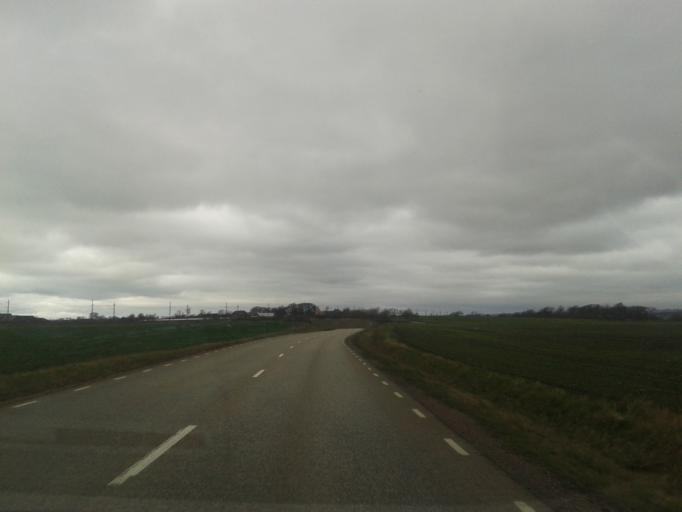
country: SE
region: Skane
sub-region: Bastads Kommun
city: Forslov
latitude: 56.3007
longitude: 12.8250
